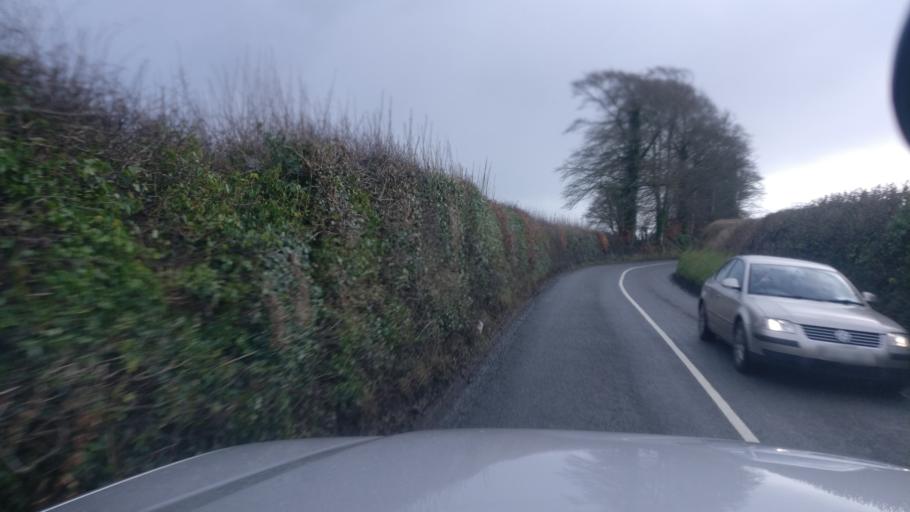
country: IE
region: Munster
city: Nenagh Bridge
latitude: 52.9675
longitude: -8.0888
